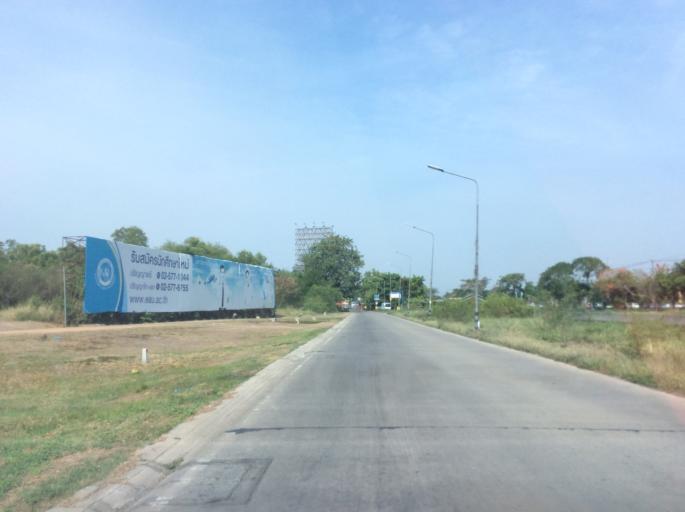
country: TH
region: Pathum Thani
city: Thanyaburi
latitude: 14.0144
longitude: 100.7228
